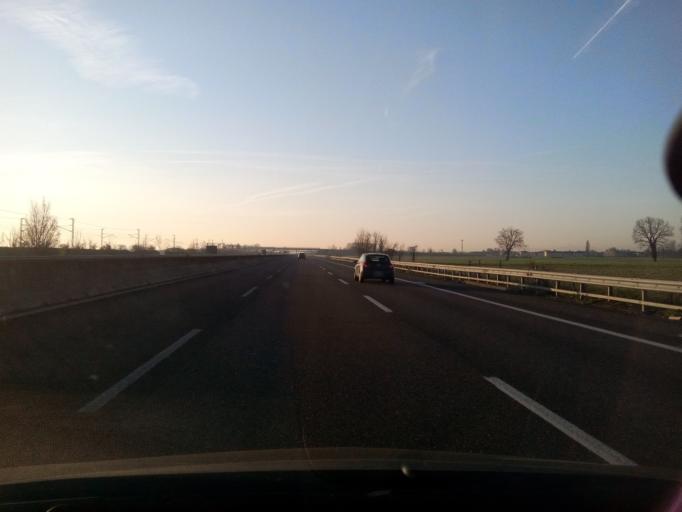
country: IT
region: Lombardy
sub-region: Provincia di Lodi
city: Livraga
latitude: 45.2039
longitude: 9.5448
